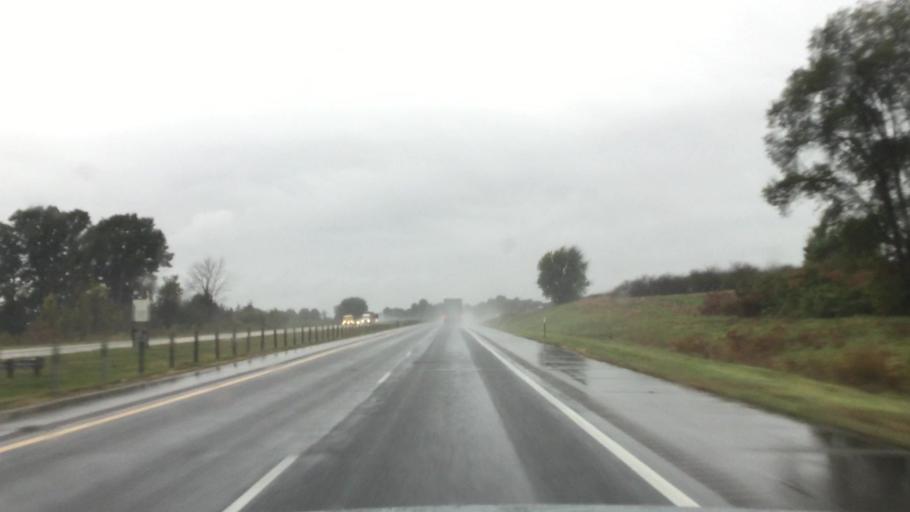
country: US
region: Michigan
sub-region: Van Buren County
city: Hartford
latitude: 42.1957
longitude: -86.1088
